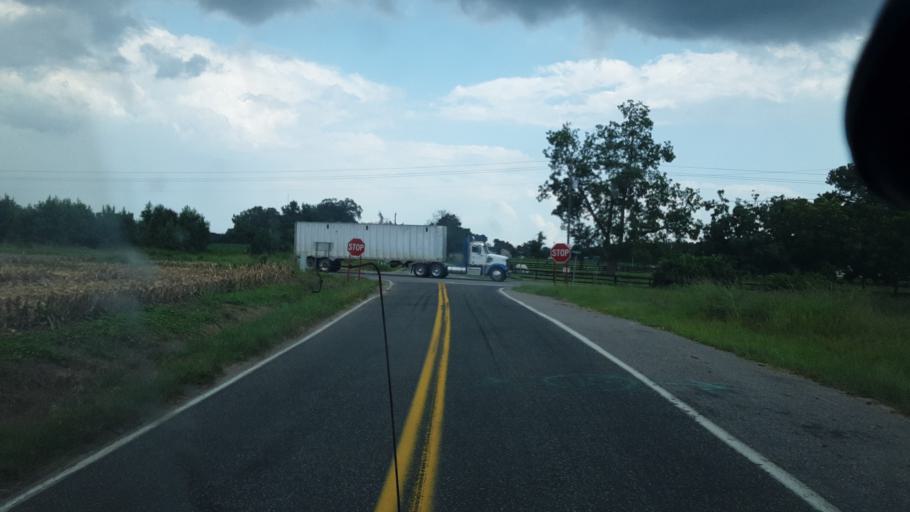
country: US
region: South Carolina
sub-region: Lee County
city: Bishopville
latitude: 34.1406
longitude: -80.1142
